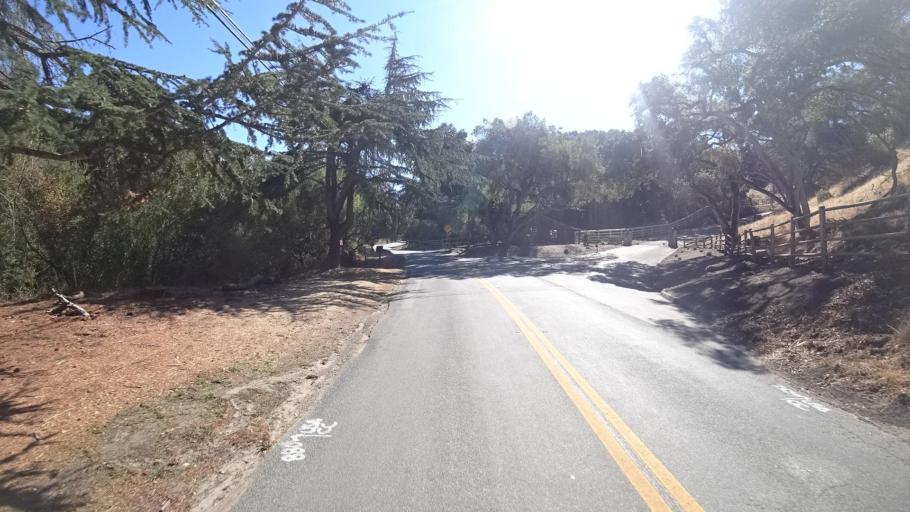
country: US
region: California
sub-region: Monterey County
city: Carmel Valley Village
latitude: 36.5305
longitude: -121.7028
